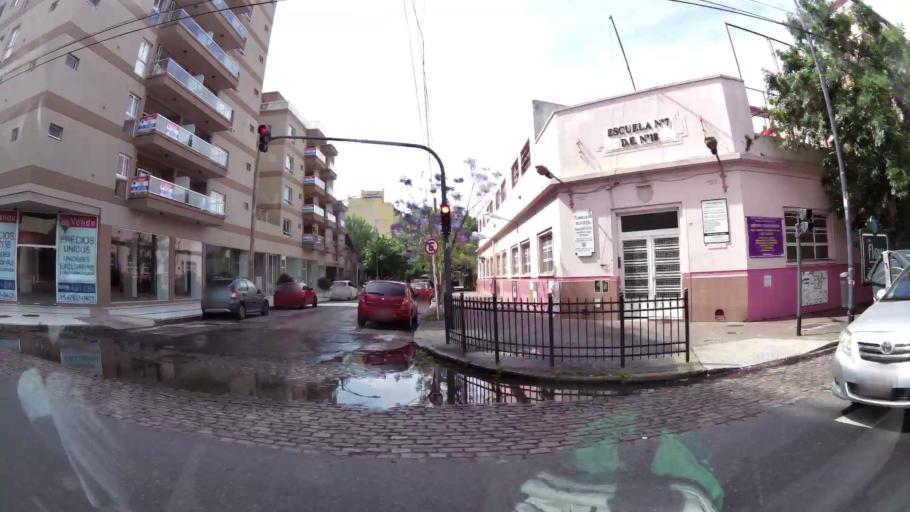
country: AR
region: Buenos Aires F.D.
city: Villa Santa Rita
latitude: -34.6378
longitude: -58.5019
